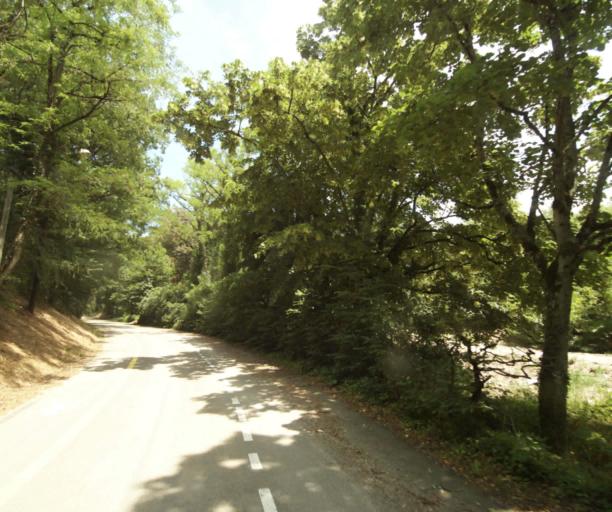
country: FR
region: Rhone-Alpes
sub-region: Departement de la Haute-Savoie
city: Chens-sur-Leman
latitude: 46.3246
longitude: 6.2618
